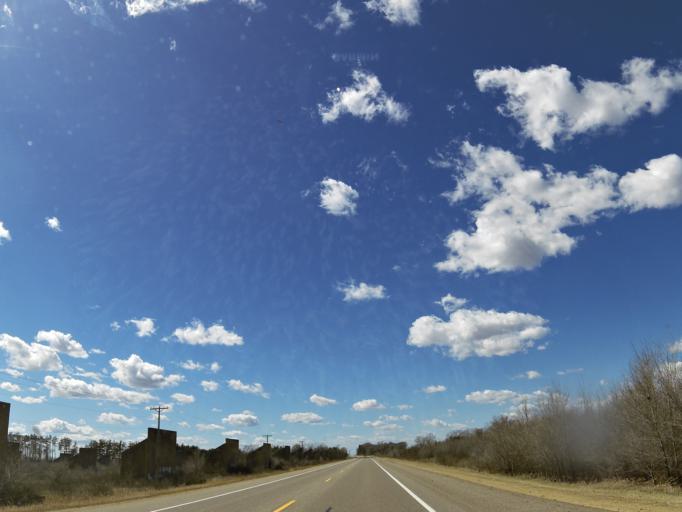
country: US
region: Minnesota
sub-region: Dakota County
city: Rosemount
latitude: 44.7178
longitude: -93.0784
